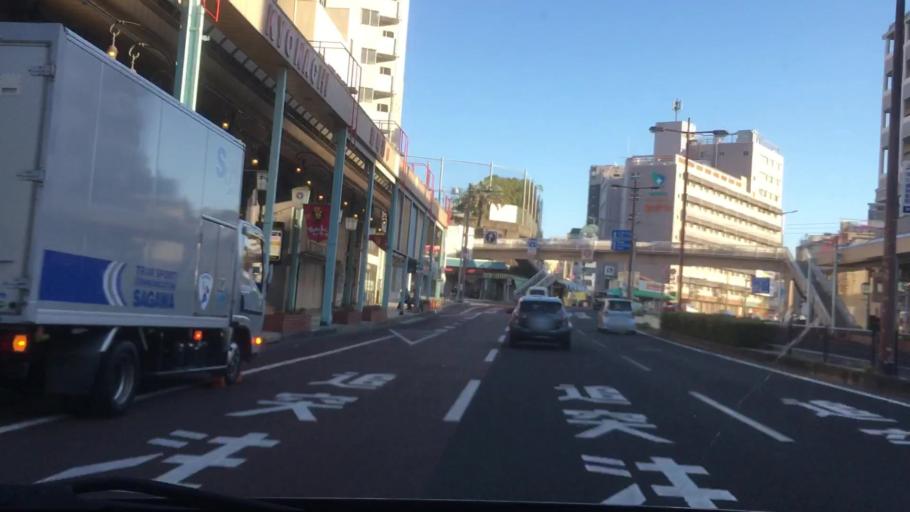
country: JP
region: Nagasaki
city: Sasebo
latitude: 33.1695
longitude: 129.7236
